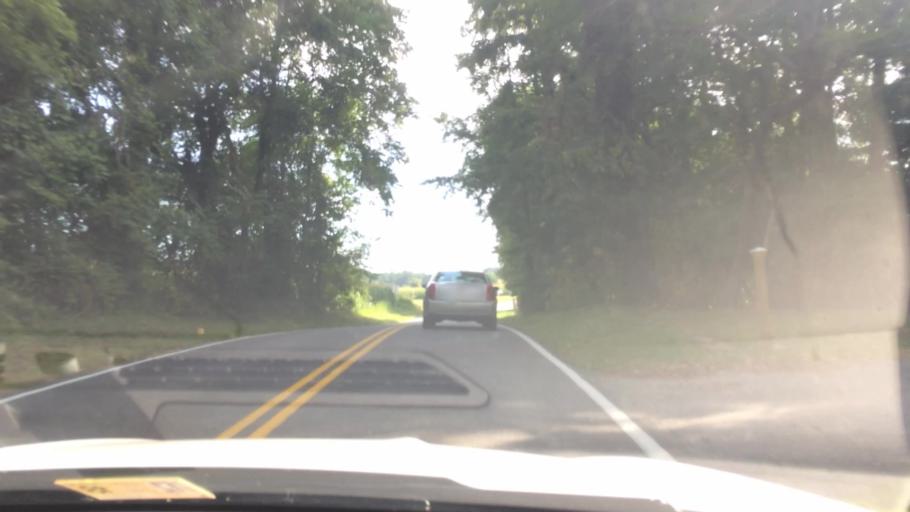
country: US
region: Virginia
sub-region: King William County
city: West Point
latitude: 37.4758
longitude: -76.8228
